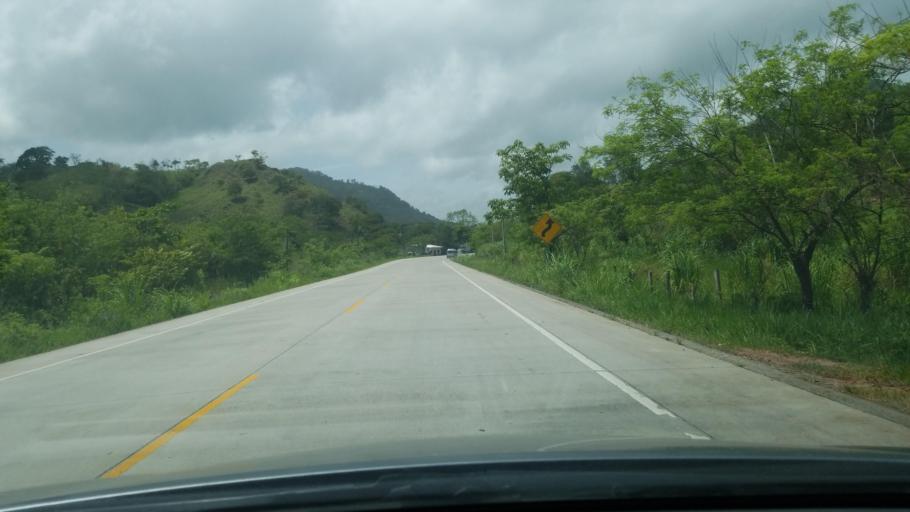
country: HN
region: Copan
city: Trinidad de Copan
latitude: 14.9585
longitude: -88.7707
